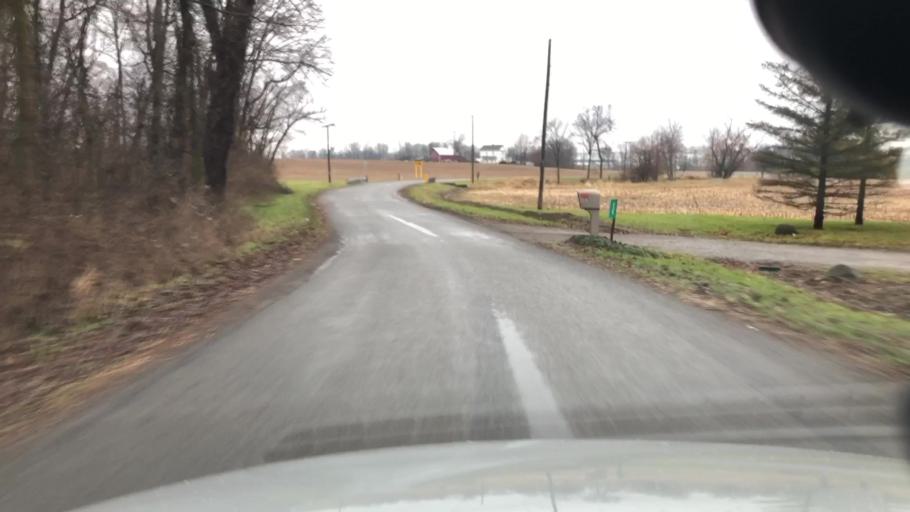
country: US
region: Ohio
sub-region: Allen County
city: Lima
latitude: 40.7385
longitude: -83.9932
